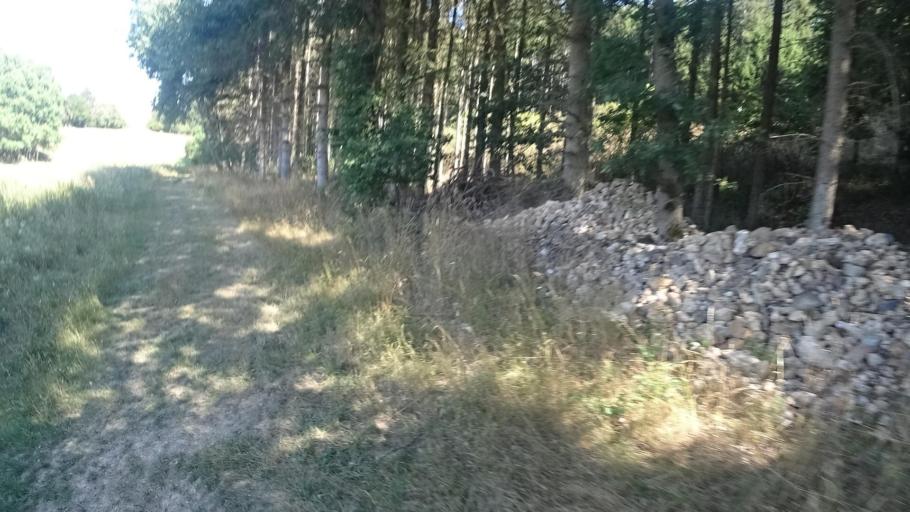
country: DE
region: Rheinland-Pfalz
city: Nannhausen
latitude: 49.9605
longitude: 7.4829
